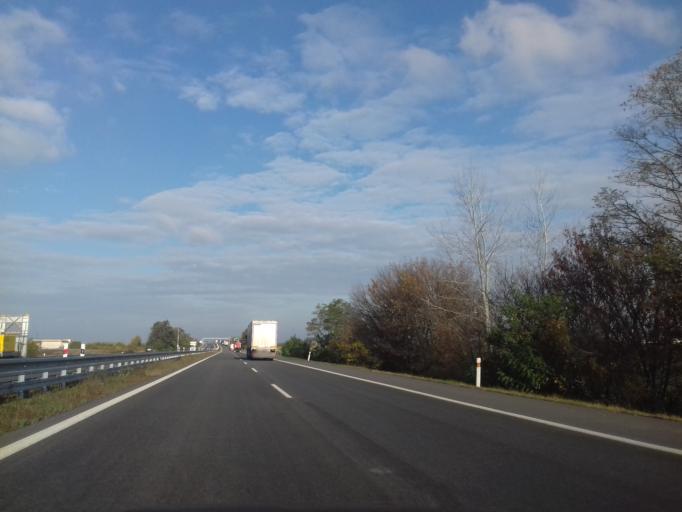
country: CZ
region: South Moravian
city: Hrusky
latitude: 48.7729
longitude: 16.9359
